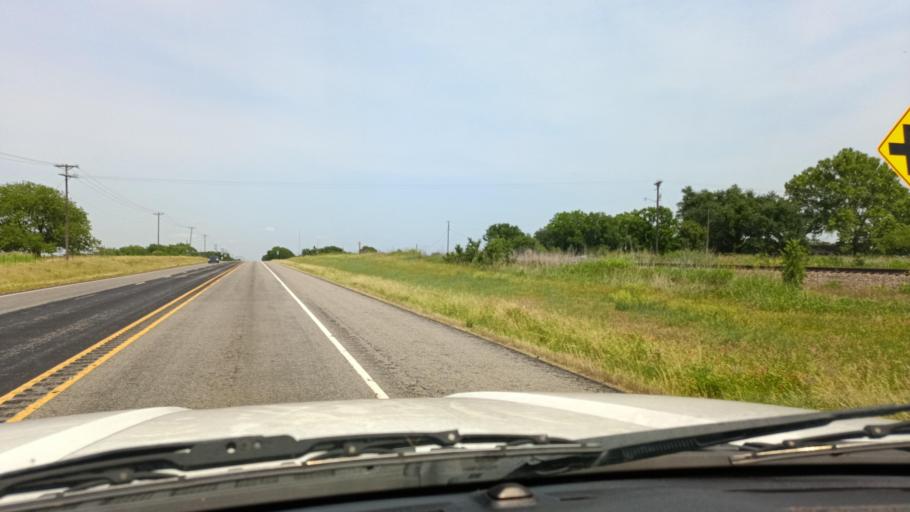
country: US
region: Texas
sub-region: Milam County
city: Cameron
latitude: 30.8488
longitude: -97.0538
